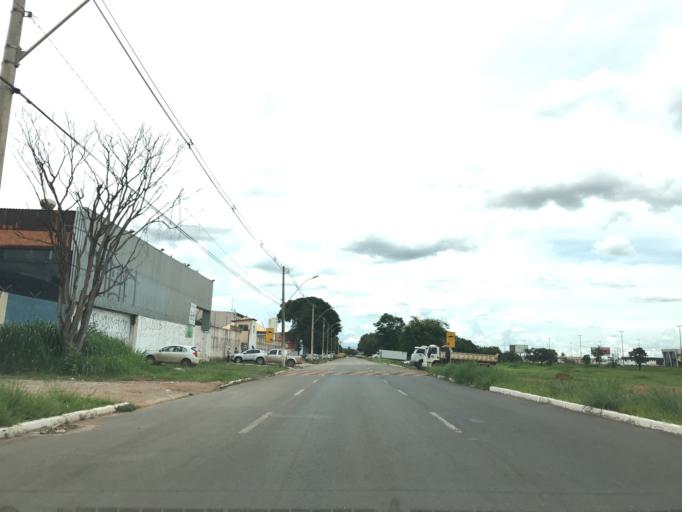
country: BR
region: Federal District
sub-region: Brasilia
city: Brasilia
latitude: -15.7896
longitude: -47.9847
